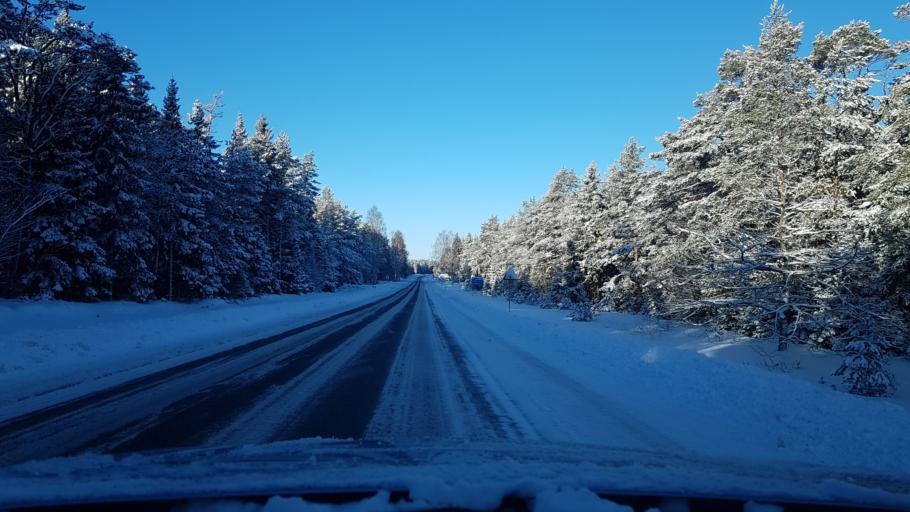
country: EE
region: Hiiumaa
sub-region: Kaerdla linn
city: Kardla
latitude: 58.9614
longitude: 22.8480
